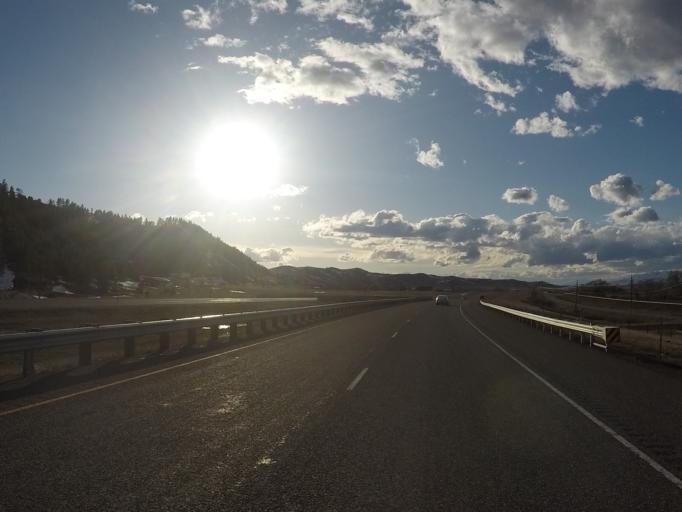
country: US
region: Montana
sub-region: Stillwater County
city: Absarokee
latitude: 45.7065
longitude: -109.6064
